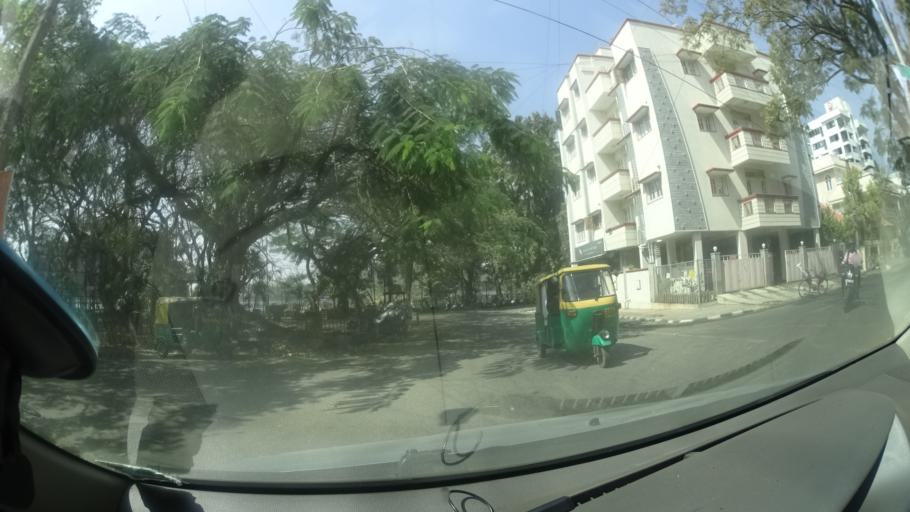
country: IN
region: Karnataka
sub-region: Bangalore Urban
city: Bangalore
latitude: 13.0095
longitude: 77.5762
